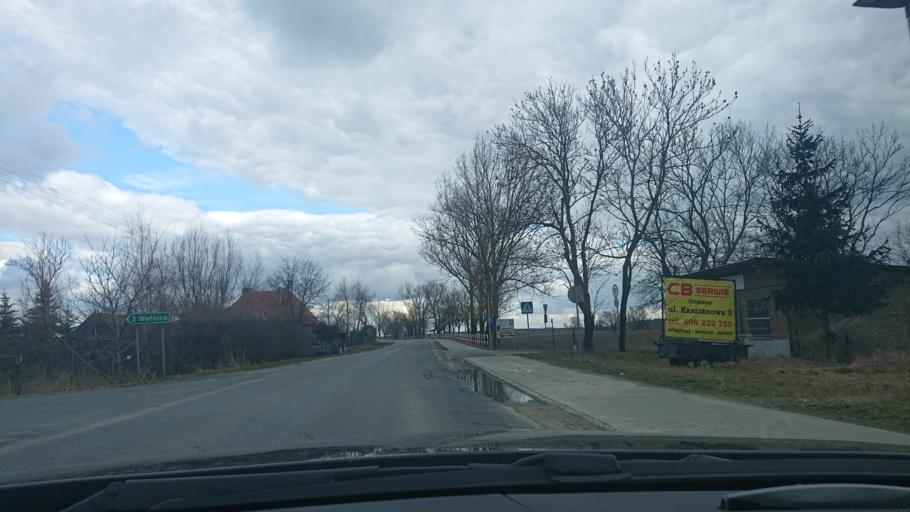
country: PL
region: Greater Poland Voivodeship
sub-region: Powiat gnieznienski
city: Gniezno
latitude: 52.5453
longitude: 17.6624
